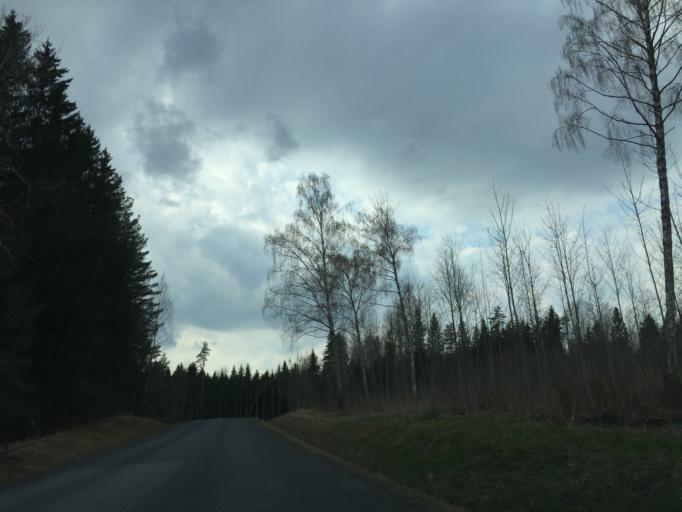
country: RU
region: Pskov
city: Pechory
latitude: 57.7338
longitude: 27.3308
